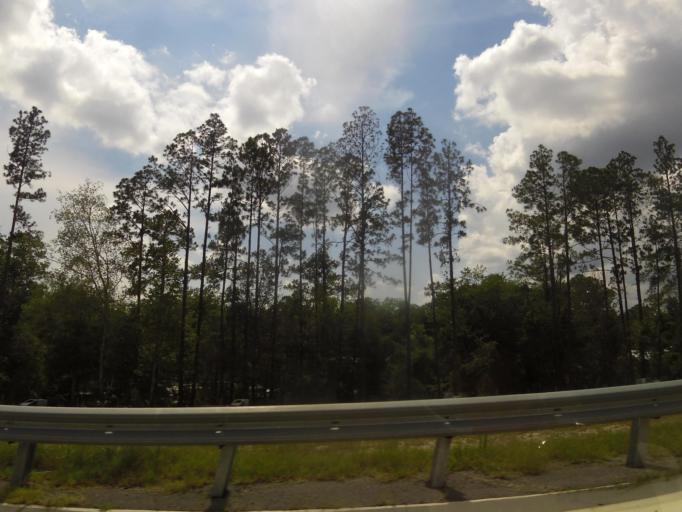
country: US
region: Florida
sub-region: Duval County
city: Baldwin
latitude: 30.3076
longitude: -81.9893
